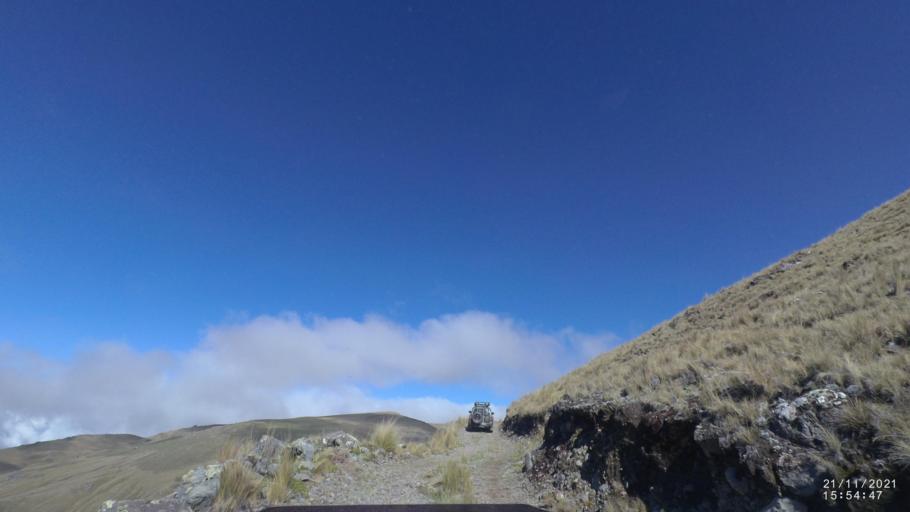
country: BO
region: Cochabamba
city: Cochabamba
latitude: -16.9728
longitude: -66.2667
